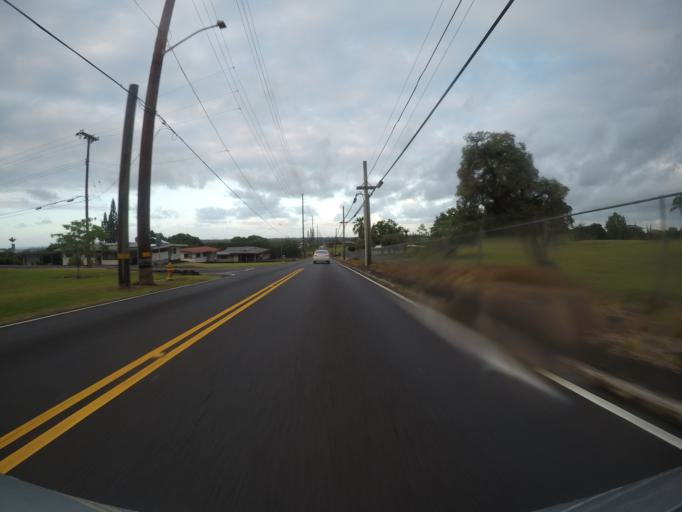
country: US
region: Hawaii
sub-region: Hawaii County
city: Hilo
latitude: 19.6840
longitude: -155.0780
